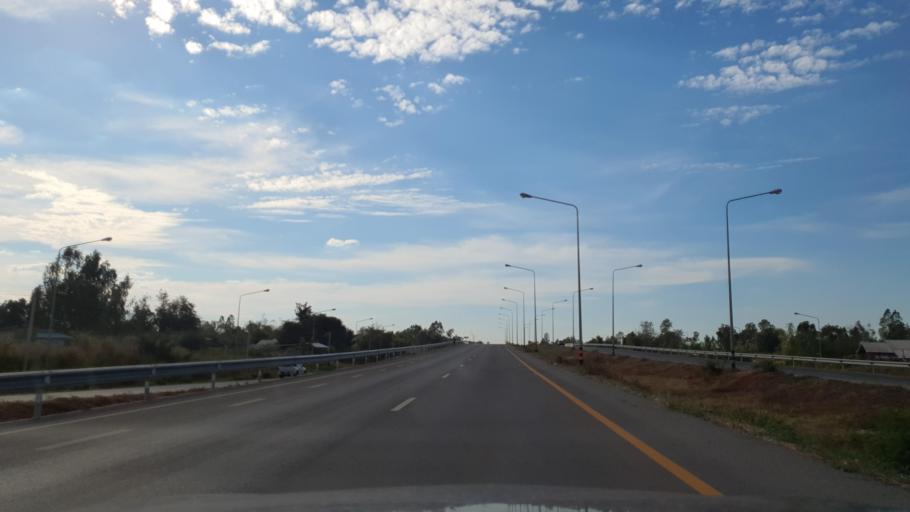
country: TH
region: Kalasin
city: Don Chan
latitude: 16.4119
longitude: 103.7593
